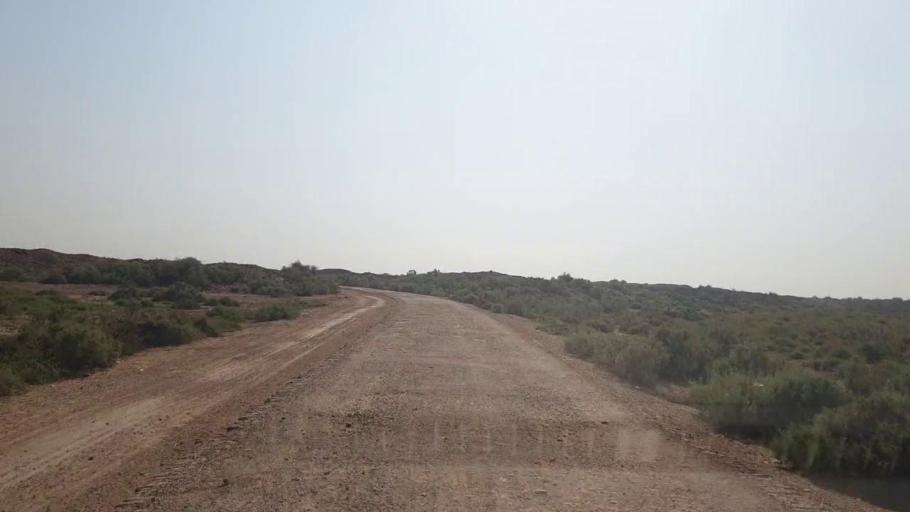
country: PK
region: Sindh
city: Berani
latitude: 25.8823
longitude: 68.7712
